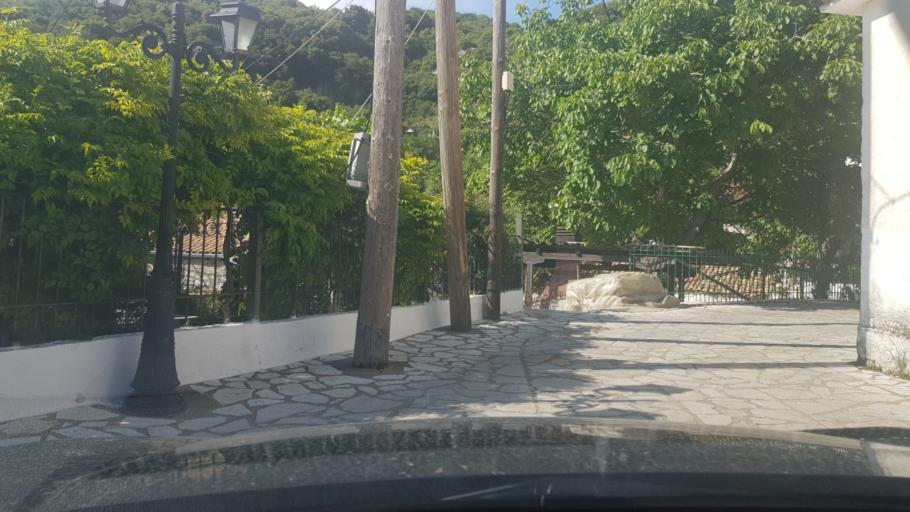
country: GR
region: Ionian Islands
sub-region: Lefkada
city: Nidri
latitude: 38.6900
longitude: 20.6456
